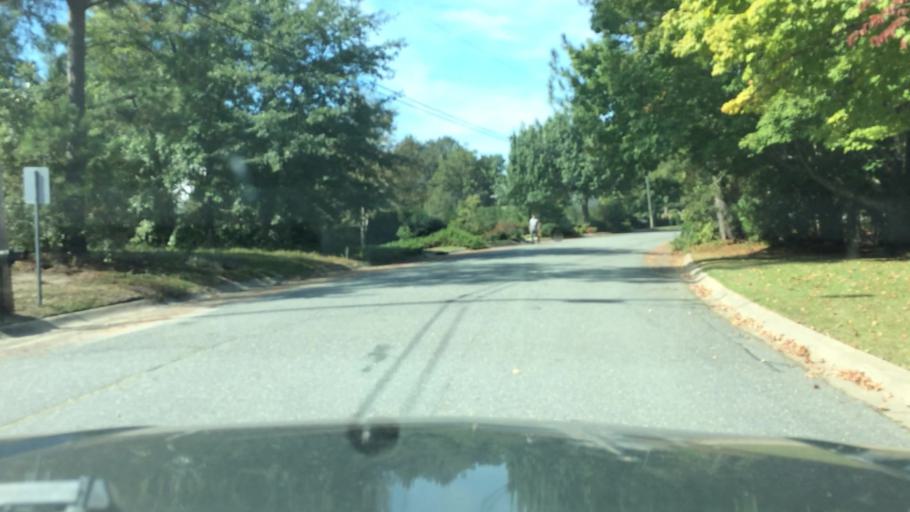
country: US
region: North Carolina
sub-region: Wayne County
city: Goldsboro
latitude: 35.3940
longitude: -77.9584
